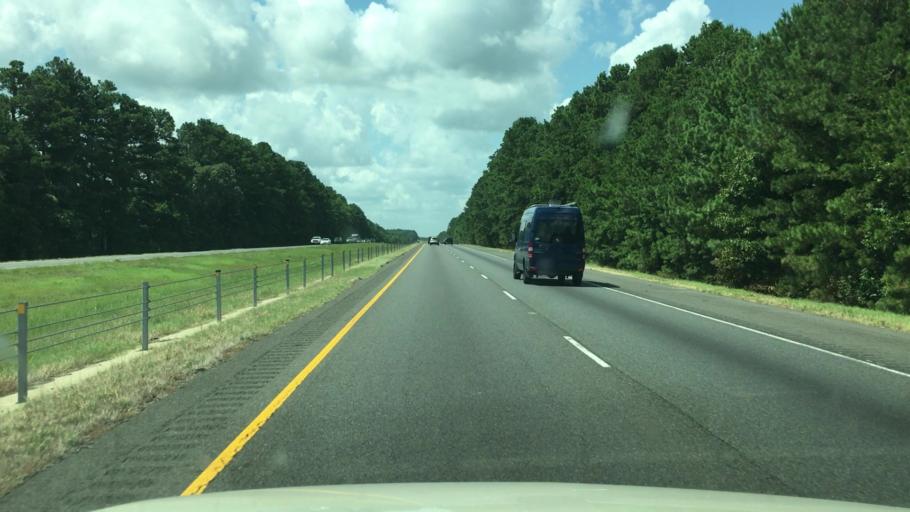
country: US
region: Arkansas
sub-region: Clark County
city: Arkadelphia
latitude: 34.0613
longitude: -93.1277
